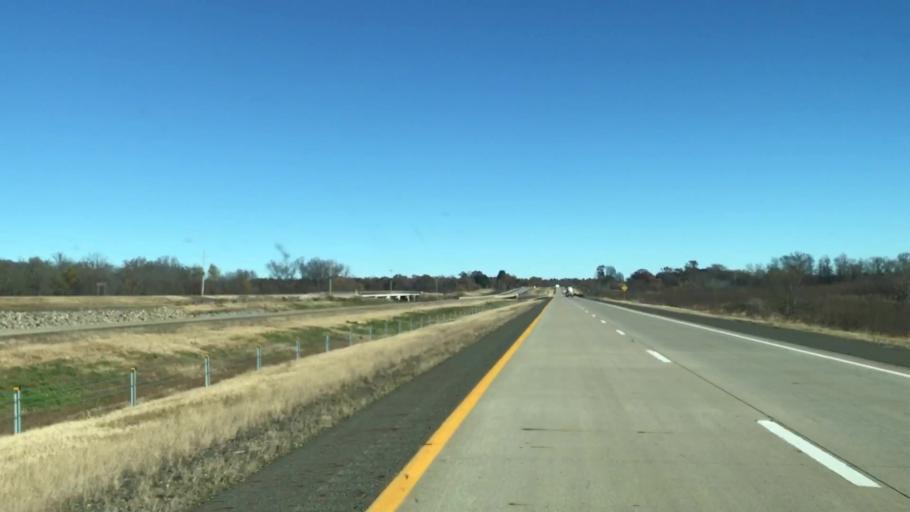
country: US
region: Texas
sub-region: Cass County
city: Queen City
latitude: 33.1455
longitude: -93.8920
